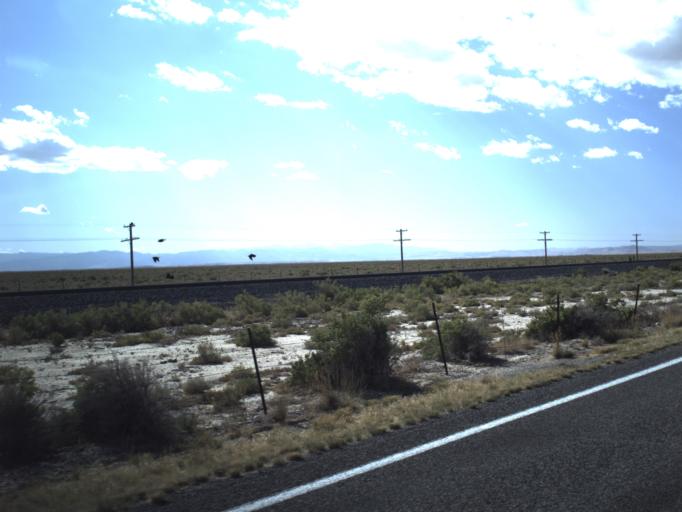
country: US
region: Utah
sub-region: Millard County
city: Delta
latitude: 39.0875
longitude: -112.7526
